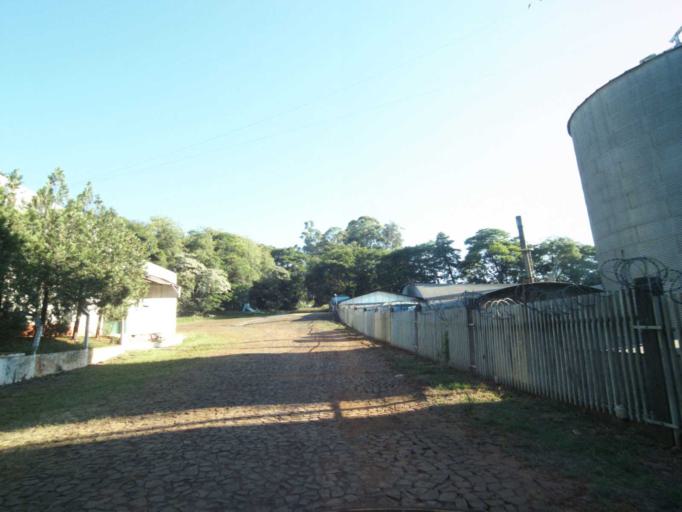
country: BR
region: Parana
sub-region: Coronel Vivida
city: Coronel Vivida
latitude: -25.9713
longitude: -52.8119
